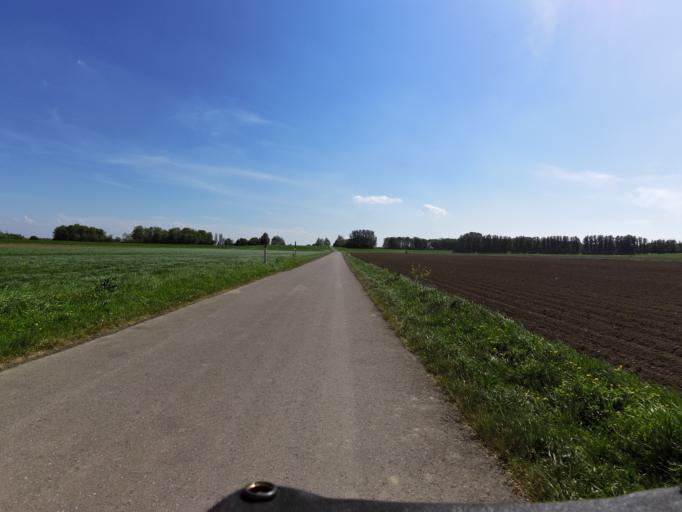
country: NL
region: South Holland
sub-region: Gemeente Binnenmaas
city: Heinenoord
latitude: 51.8398
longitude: 4.4692
